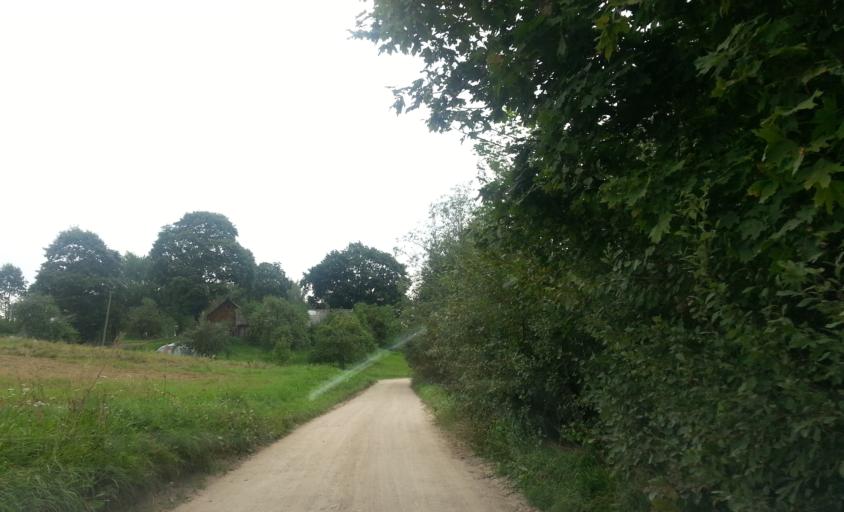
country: LT
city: Grigiskes
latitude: 54.7636
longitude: 25.0229
